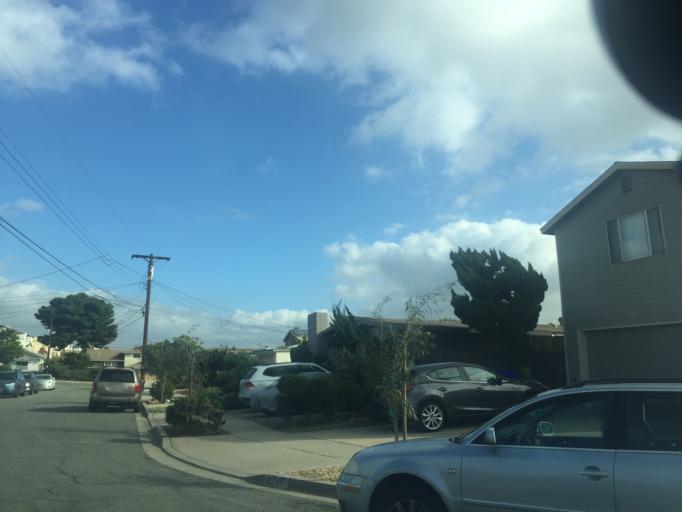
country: US
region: California
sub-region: San Diego County
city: San Diego
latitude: 32.7827
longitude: -117.1518
